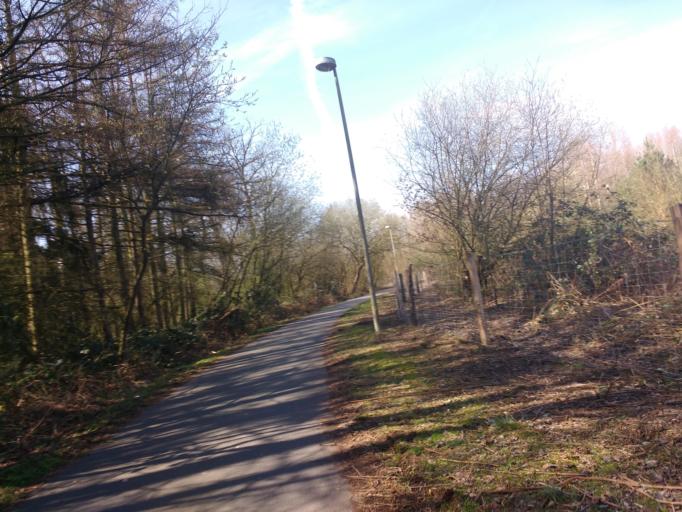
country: DE
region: North Rhine-Westphalia
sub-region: Regierungsbezirk Detmold
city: Hovelhof
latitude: 51.7537
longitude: 8.6761
